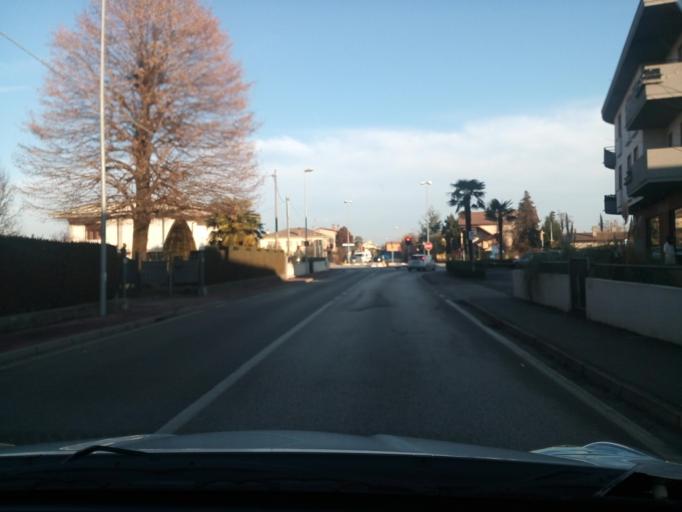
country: IT
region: Veneto
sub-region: Provincia di Vicenza
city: Dueville
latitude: 45.6413
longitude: 11.5563
